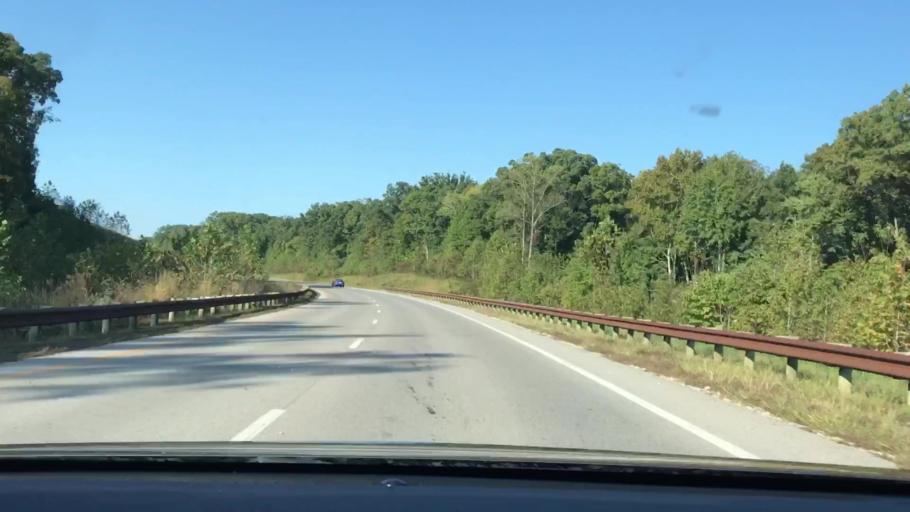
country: US
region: Kentucky
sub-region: Trigg County
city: Cadiz
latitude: 36.8029
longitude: -87.9907
